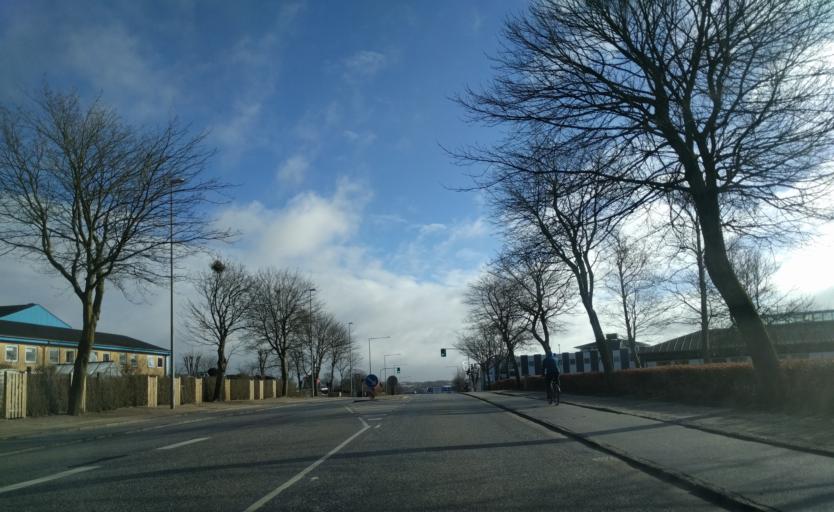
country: DK
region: North Denmark
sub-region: Alborg Kommune
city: Aalborg
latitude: 57.0232
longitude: 9.8981
